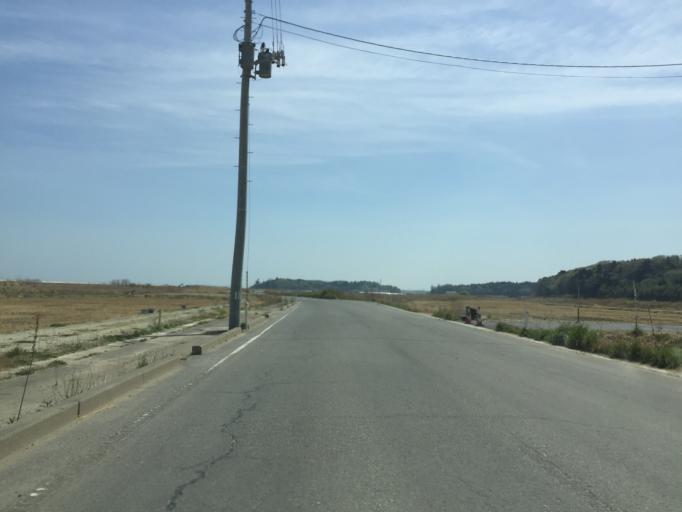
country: JP
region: Miyagi
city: Watari
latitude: 37.9119
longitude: 140.9192
